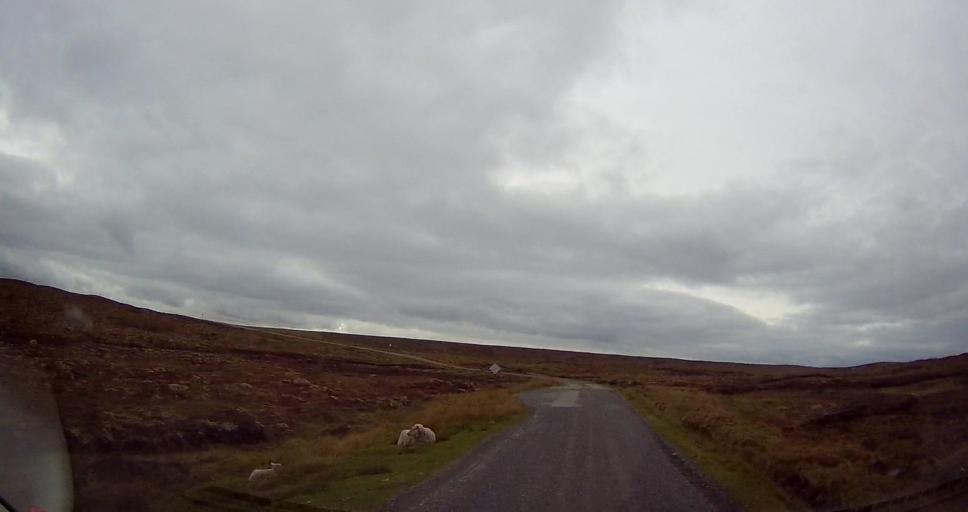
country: GB
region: Scotland
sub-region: Shetland Islands
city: Shetland
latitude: 60.5093
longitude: -1.1370
